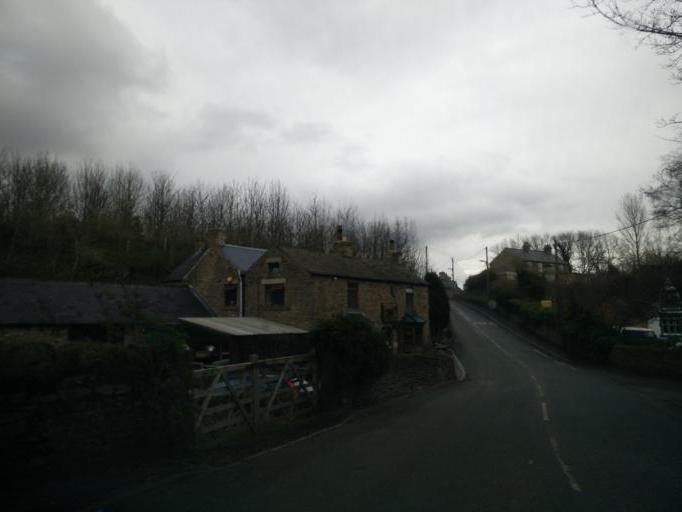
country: GB
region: England
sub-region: County Durham
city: Stanhope
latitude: 54.7273
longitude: -1.9653
